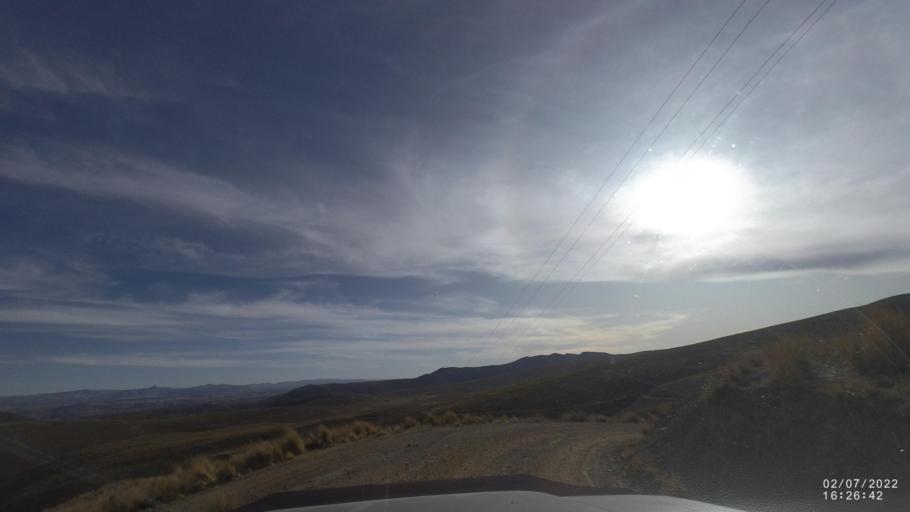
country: BO
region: Cochabamba
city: Irpa Irpa
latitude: -17.9474
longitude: -66.4672
